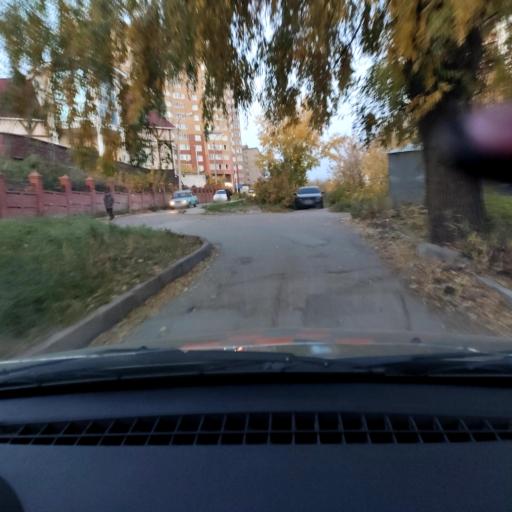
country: RU
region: Bashkortostan
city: Ufa
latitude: 54.7011
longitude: 55.9882
